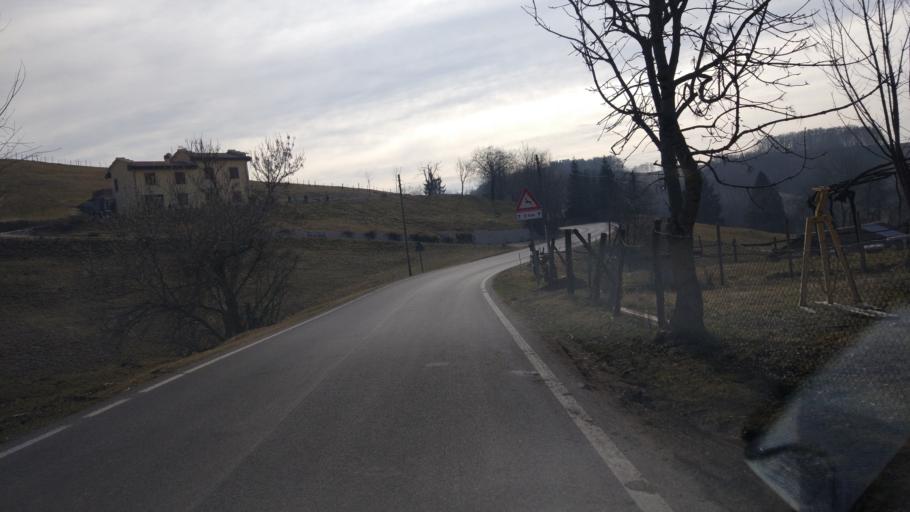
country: IT
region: Veneto
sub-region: Provincia di Verona
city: Selva di Progno
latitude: 45.6306
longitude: 11.1605
